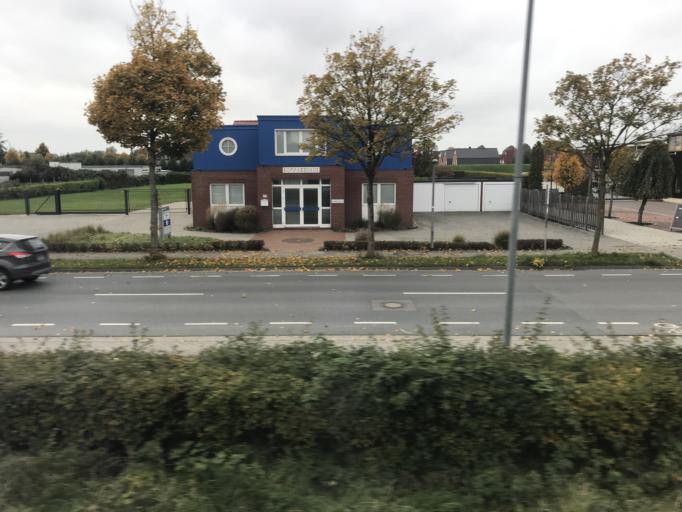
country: DE
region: Lower Saxony
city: Emden
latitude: 53.3518
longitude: 7.1916
